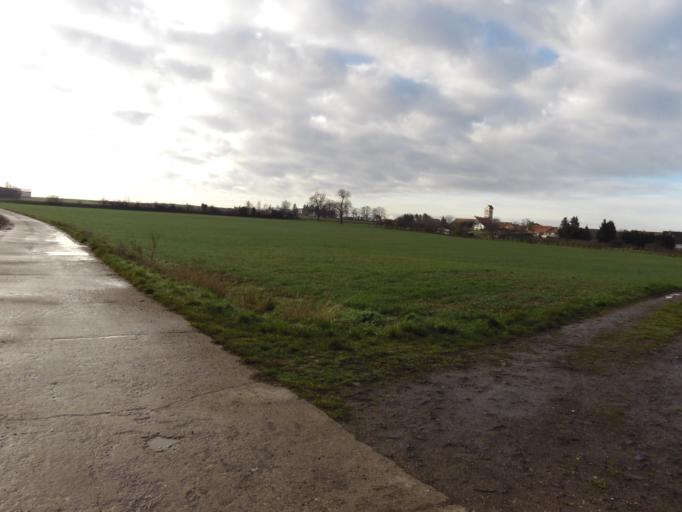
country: DE
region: Rheinland-Pfalz
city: Obrigheim
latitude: 49.5908
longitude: 8.2081
